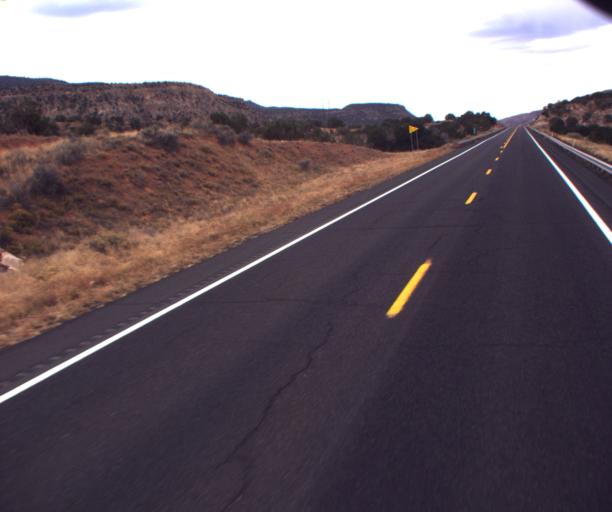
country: US
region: Arizona
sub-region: Navajo County
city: Kayenta
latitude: 36.6861
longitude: -110.3769
